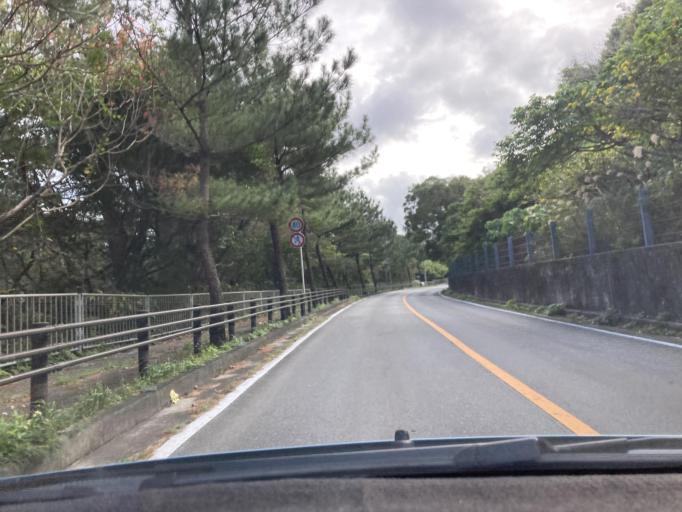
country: JP
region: Okinawa
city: Nago
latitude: 26.8600
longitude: 128.2611
